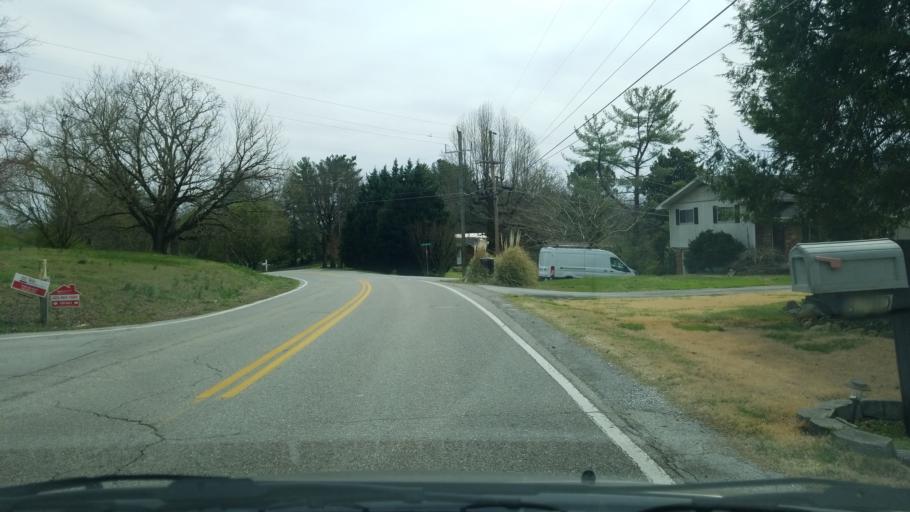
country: US
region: Tennessee
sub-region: Hamilton County
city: East Brainerd
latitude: 35.0166
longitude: -85.1191
